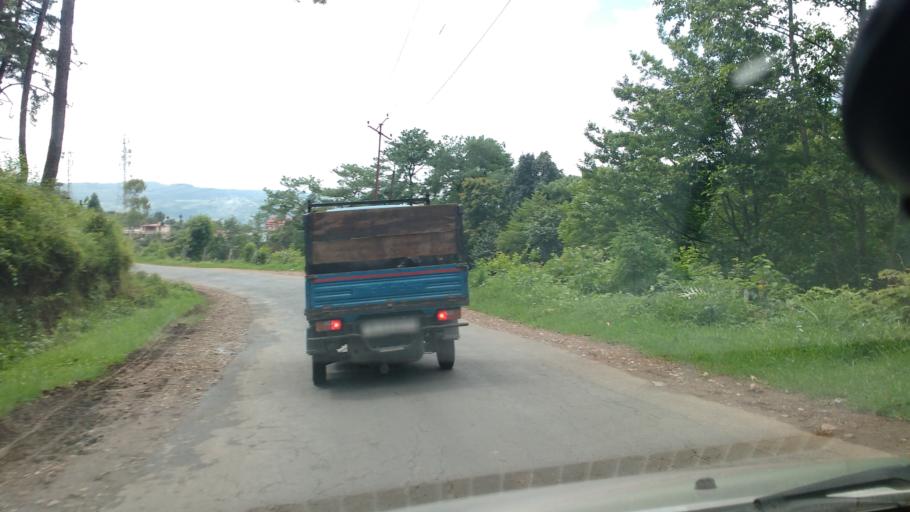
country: IN
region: Meghalaya
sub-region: East Khasi Hills
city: Shillong
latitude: 25.5485
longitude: 91.8436
